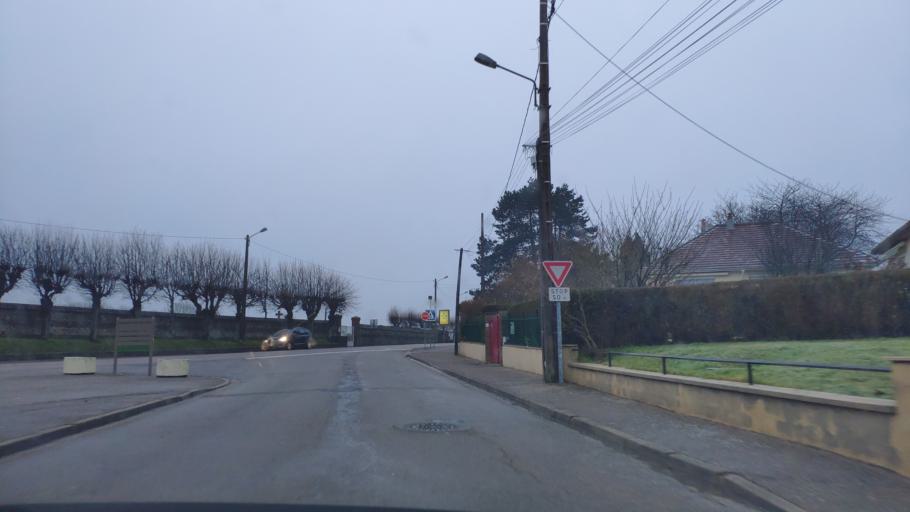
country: FR
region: Haute-Normandie
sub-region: Departement de la Seine-Maritime
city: Doudeville
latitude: 49.7240
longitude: 0.7819
